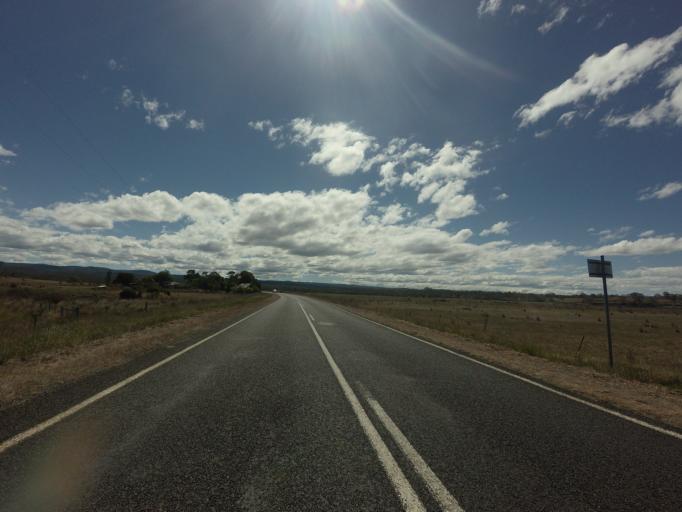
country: AU
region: Tasmania
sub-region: Break O'Day
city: St Helens
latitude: -42.0480
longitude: 148.0471
